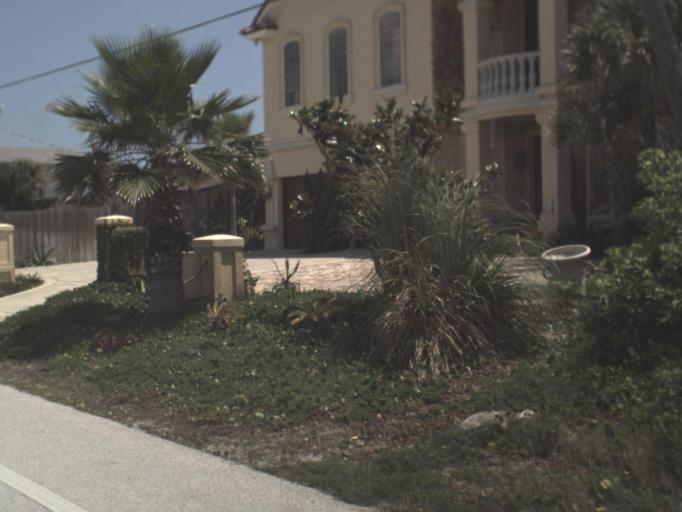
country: US
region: Florida
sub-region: Saint Johns County
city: Villano Beach
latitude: 30.0402
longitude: -81.3278
